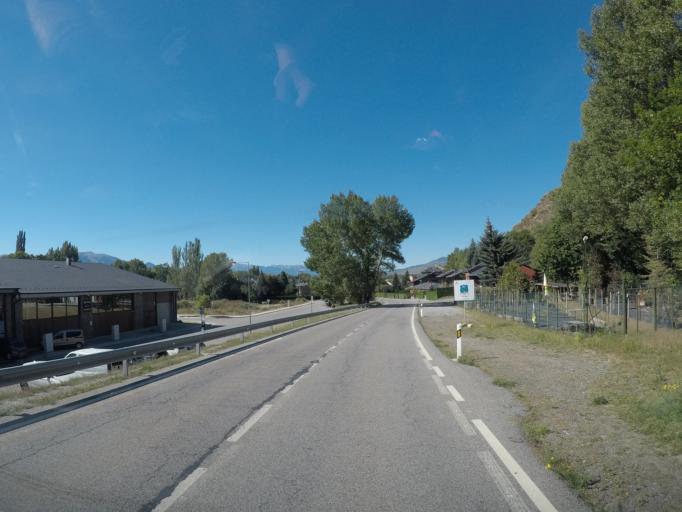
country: ES
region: Catalonia
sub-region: Provincia de Girona
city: Llivia
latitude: 42.4638
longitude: 1.9904
